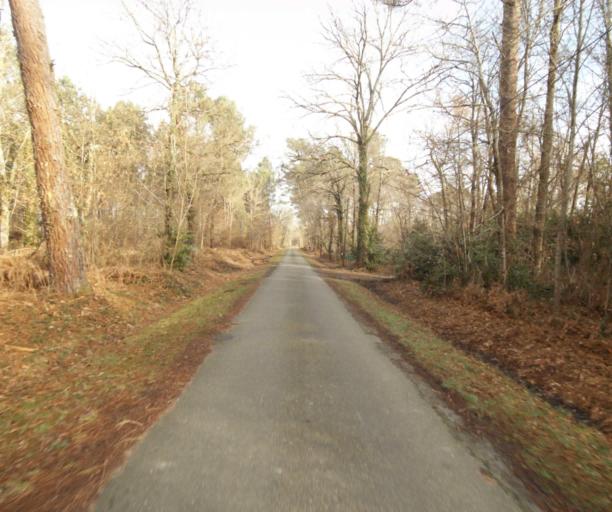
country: FR
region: Aquitaine
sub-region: Departement des Landes
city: Gabarret
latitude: 43.9931
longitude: 0.0182
